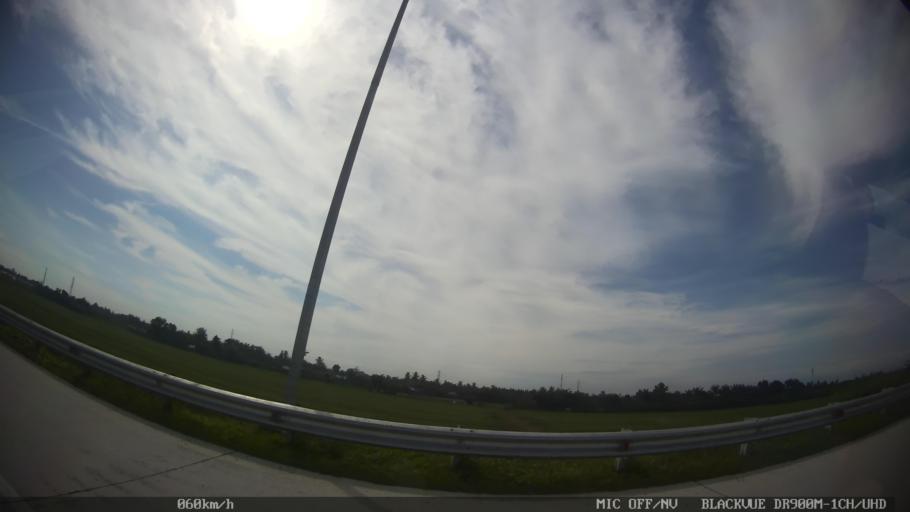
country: ID
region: North Sumatra
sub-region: Kabupaten Langkat
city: Stabat
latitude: 3.7122
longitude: 98.4955
